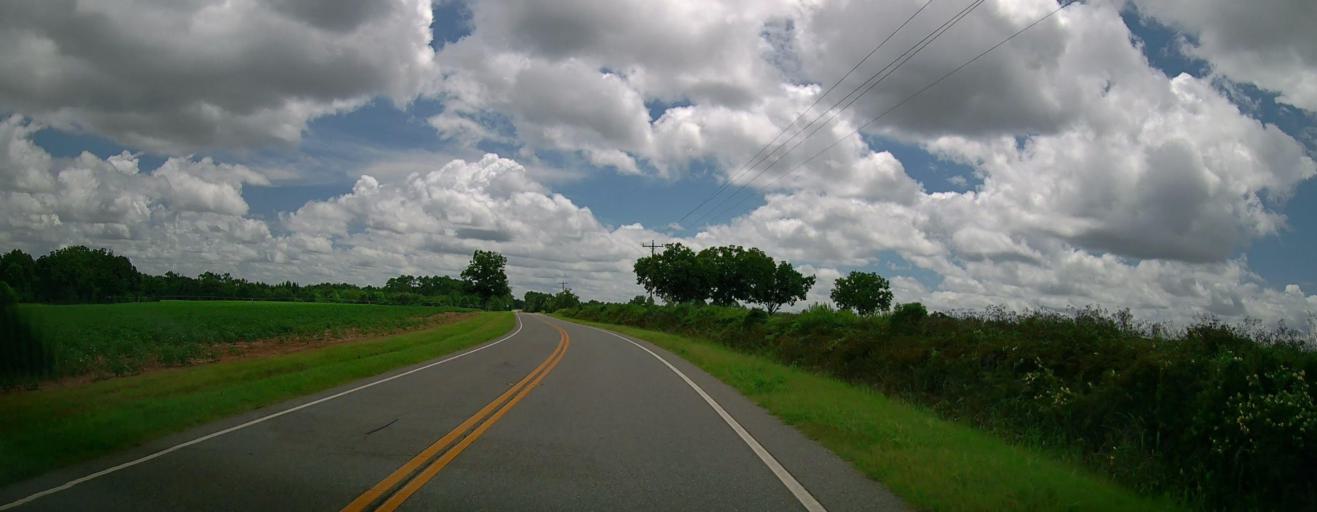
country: US
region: Georgia
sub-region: Wilcox County
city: Rochelle
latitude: 31.9691
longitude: -83.5470
